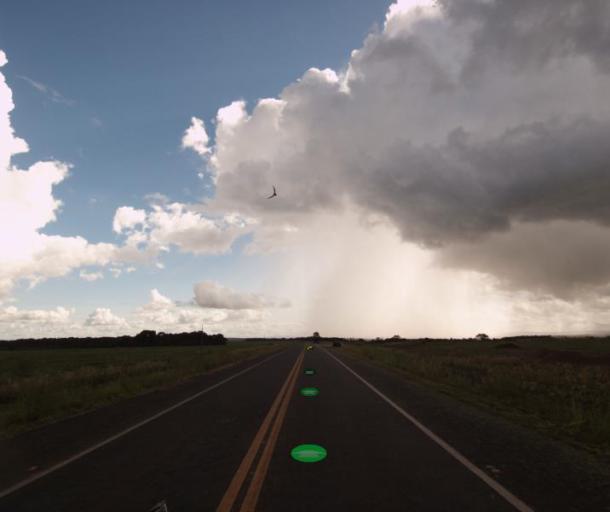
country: BR
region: Goias
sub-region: Itaberai
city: Itaberai
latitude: -15.9902
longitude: -49.7223
